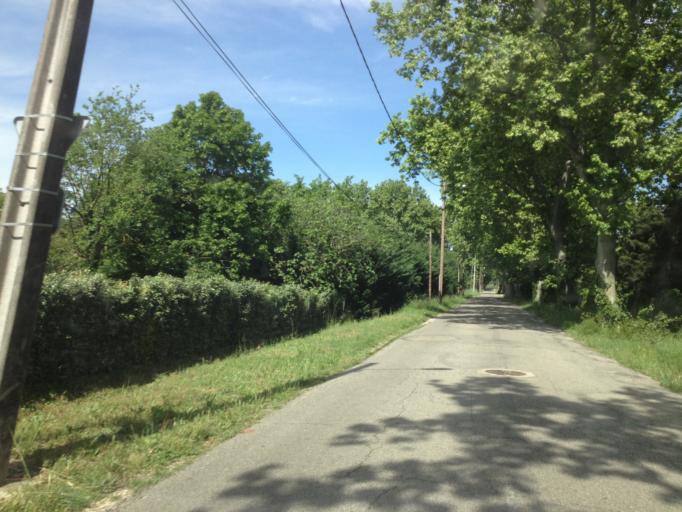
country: FR
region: Provence-Alpes-Cote d'Azur
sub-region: Departement du Vaucluse
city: Sorgues
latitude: 43.9968
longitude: 4.8674
